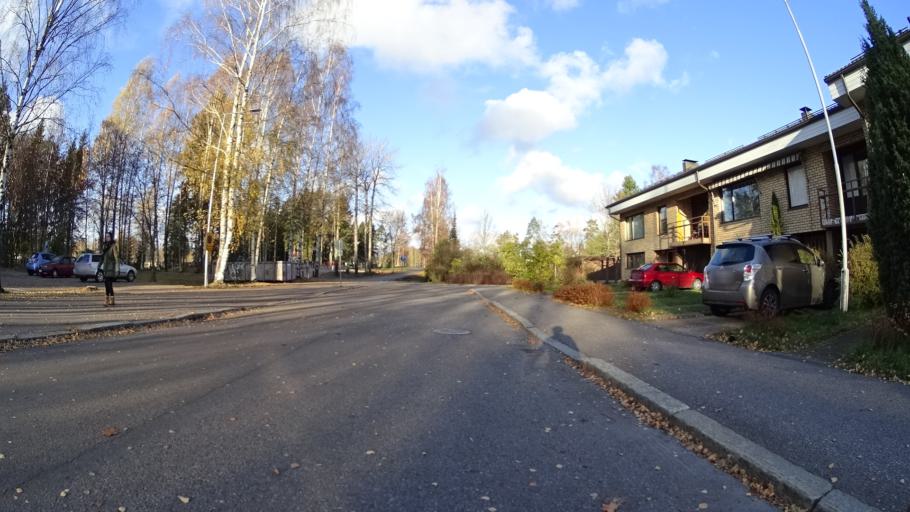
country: FI
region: Uusimaa
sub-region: Helsinki
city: Kilo
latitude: 60.2598
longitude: 24.8294
